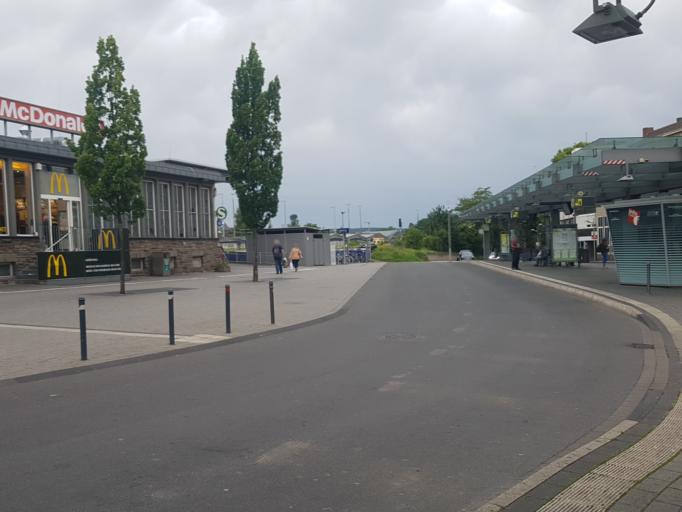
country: DE
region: North Rhine-Westphalia
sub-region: Regierungsbezirk Koln
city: Euskirchen
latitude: 50.6584
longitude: 6.7920
